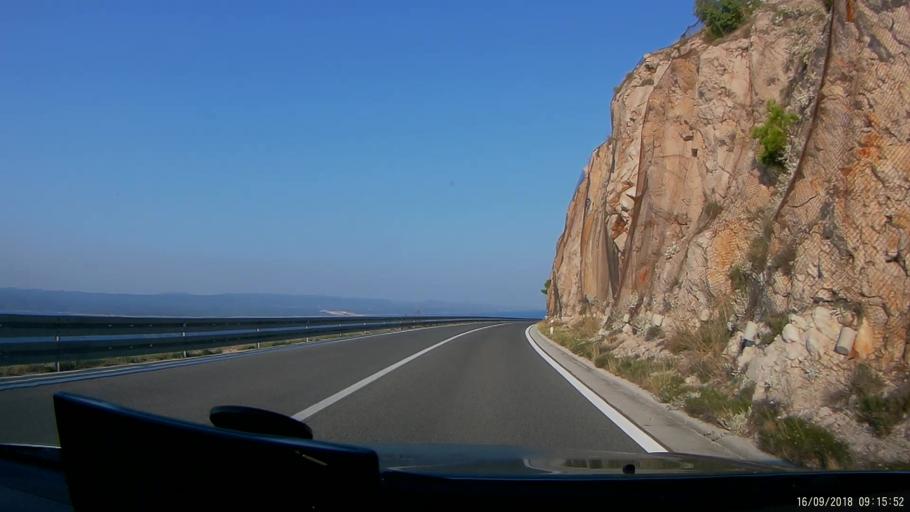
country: HR
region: Splitsko-Dalmatinska
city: Donja Brela
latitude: 43.3998
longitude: 16.8744
